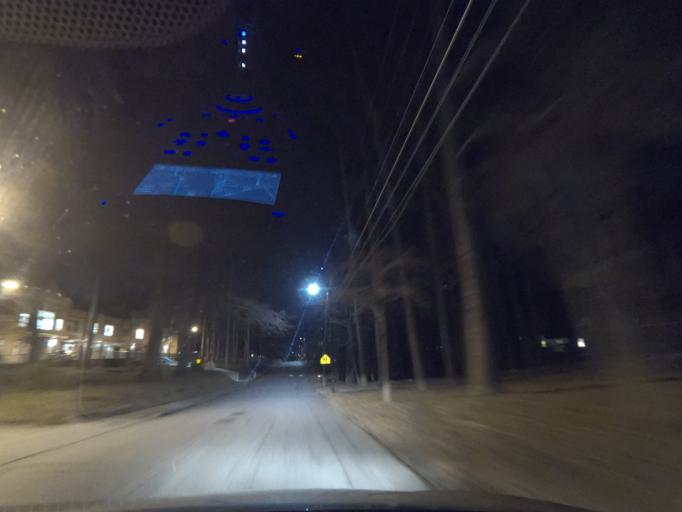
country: US
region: Georgia
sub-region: Cobb County
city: Vinings
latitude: 33.8168
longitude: -84.4548
